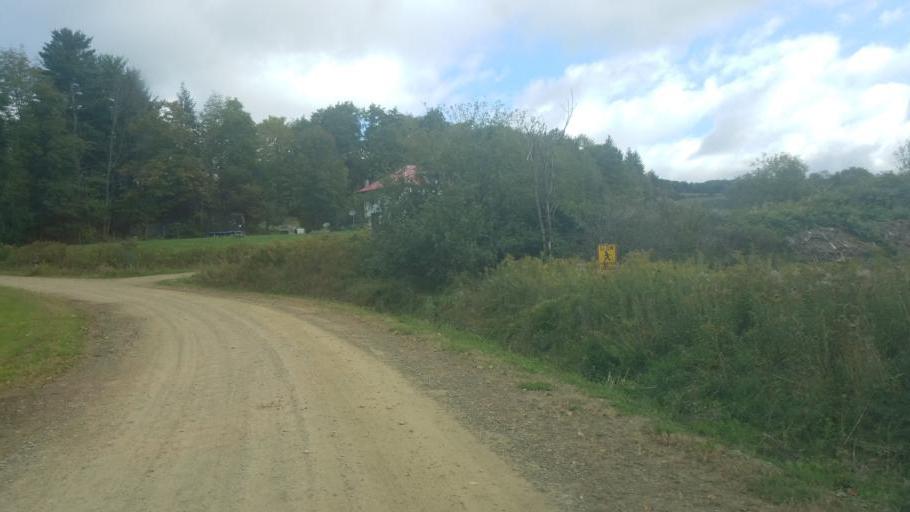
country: US
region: New York
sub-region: Allegany County
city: Cuba
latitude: 42.1320
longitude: -78.3007
